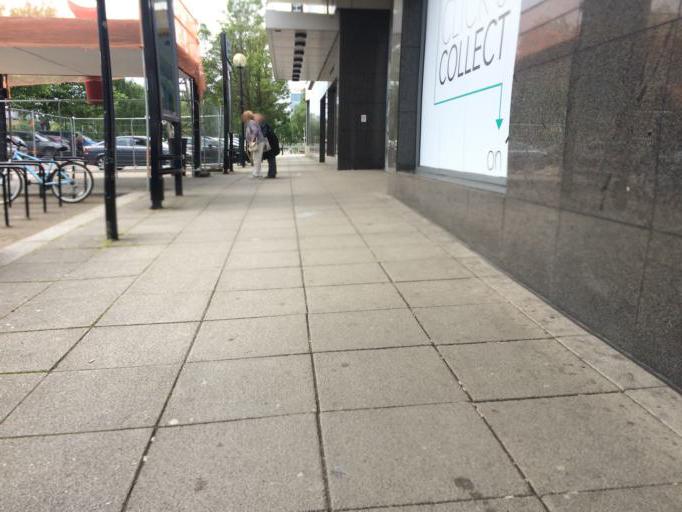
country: GB
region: England
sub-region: Milton Keynes
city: Milton Keynes
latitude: 52.0399
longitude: -0.7566
